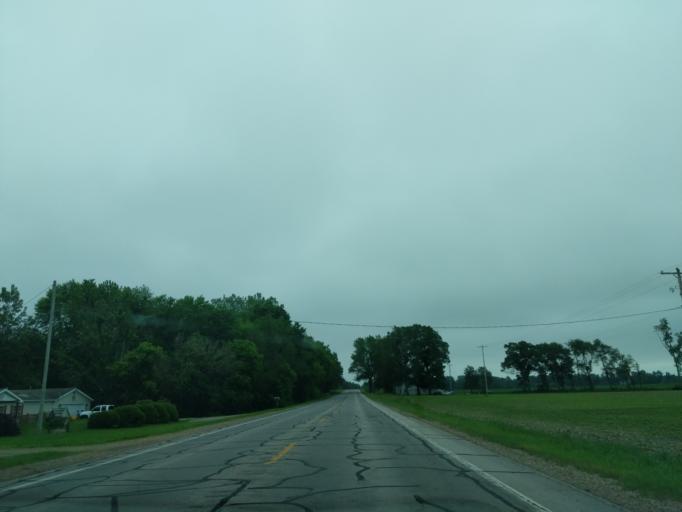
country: US
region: Michigan
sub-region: Hillsdale County
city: Litchfield
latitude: 42.0675
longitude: -84.7895
